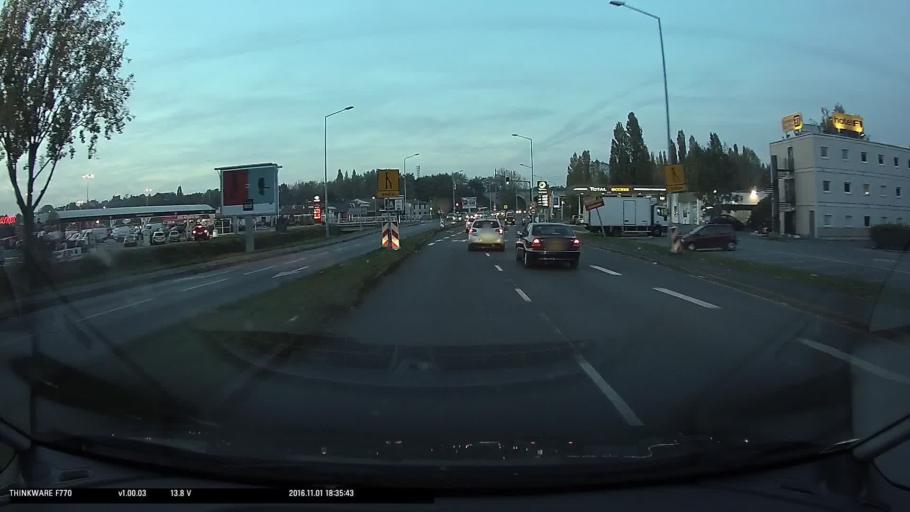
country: FR
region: Ile-de-France
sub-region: Departement de l'Essonne
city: Villemoisson-sur-Orge
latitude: 48.6678
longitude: 2.3387
